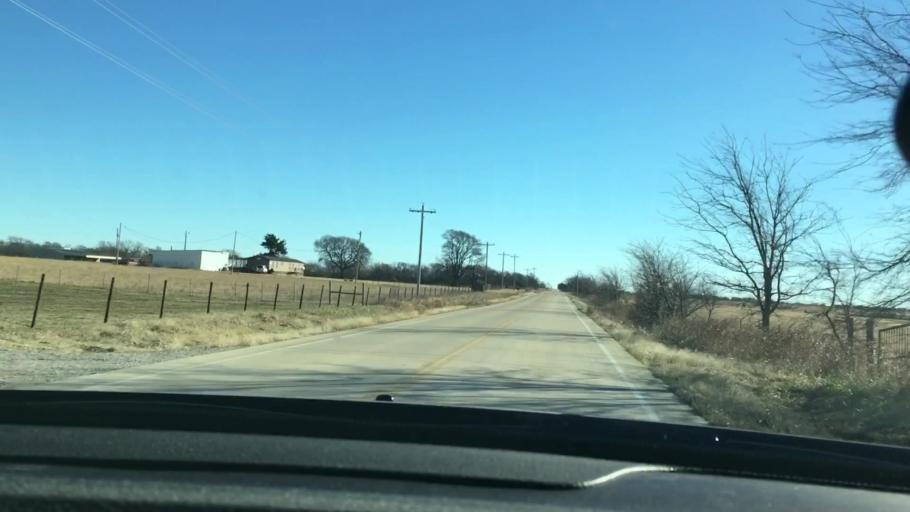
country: US
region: Oklahoma
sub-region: Marshall County
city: Madill
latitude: 34.1144
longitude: -96.6844
